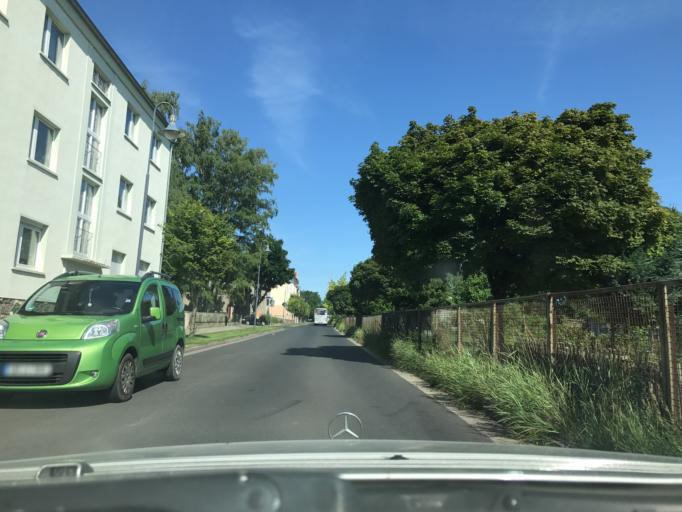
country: DE
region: Thuringia
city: Muehlhausen
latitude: 51.2067
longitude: 10.4759
